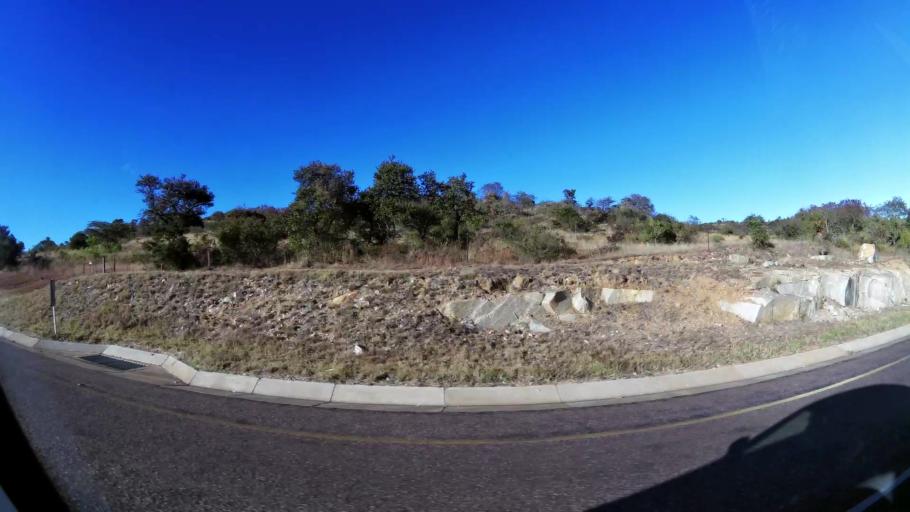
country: ZA
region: Limpopo
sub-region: Capricorn District Municipality
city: Mankoeng
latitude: -23.9232
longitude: 29.8907
